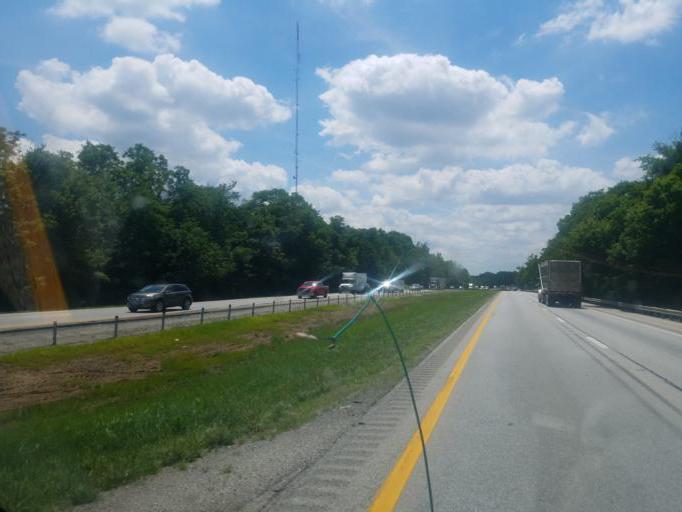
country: US
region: Kentucky
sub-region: Jefferson County
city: Worthington
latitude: 38.3269
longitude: -85.5482
